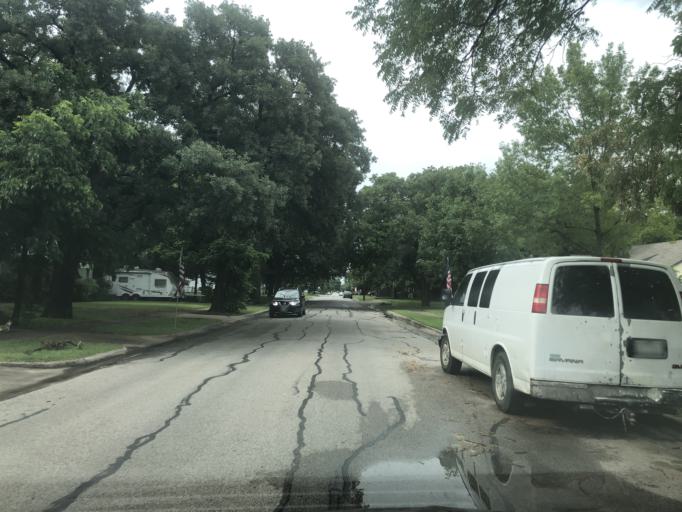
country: US
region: Texas
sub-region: Dallas County
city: Irving
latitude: 32.8103
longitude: -96.9437
